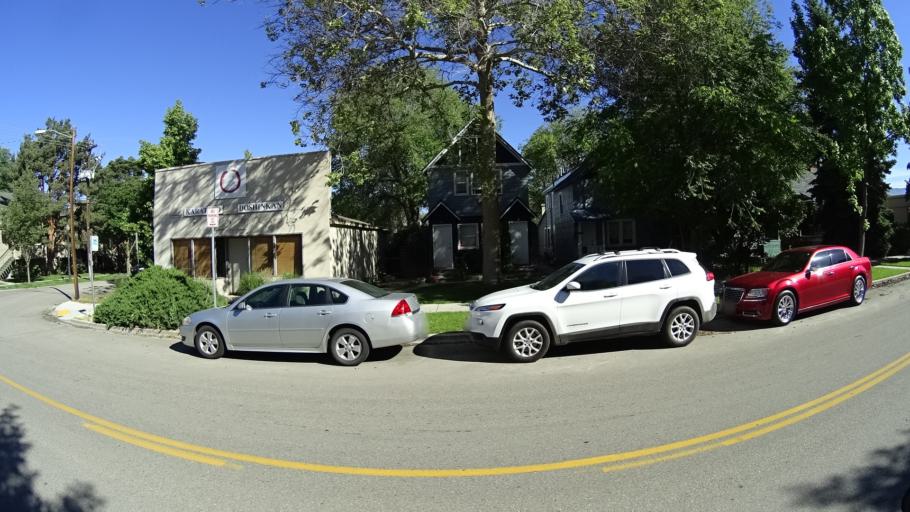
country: US
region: Idaho
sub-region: Ada County
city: Boise
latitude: 43.6158
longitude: -116.2128
